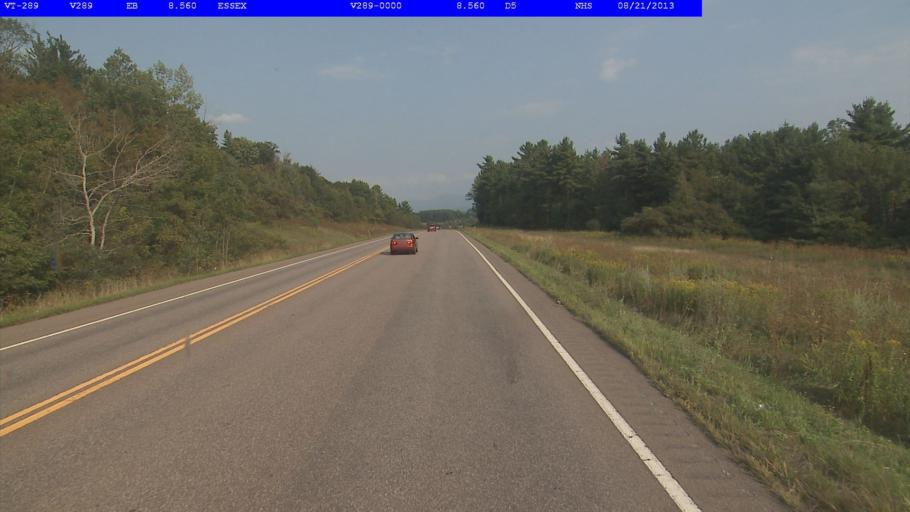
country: US
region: Vermont
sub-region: Chittenden County
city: Essex Junction
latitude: 44.5141
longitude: -73.1031
